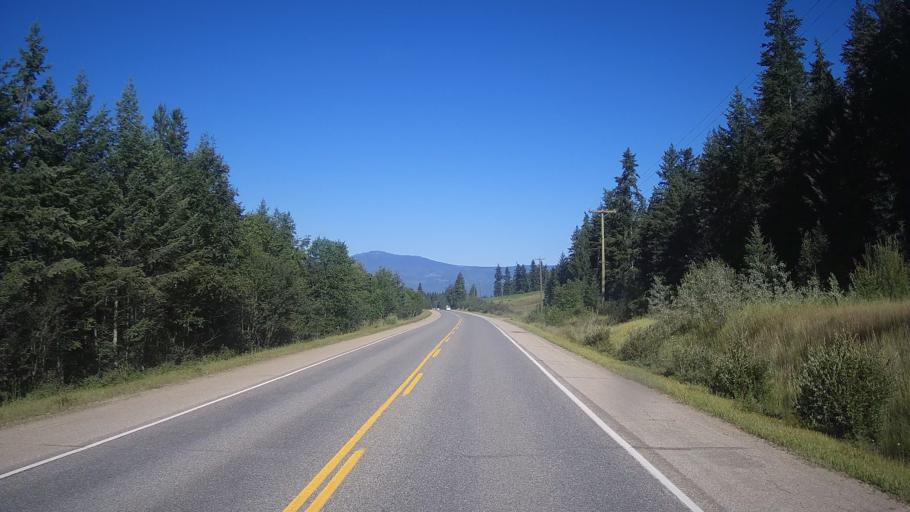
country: CA
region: British Columbia
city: Chase
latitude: 51.6032
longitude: -119.8946
